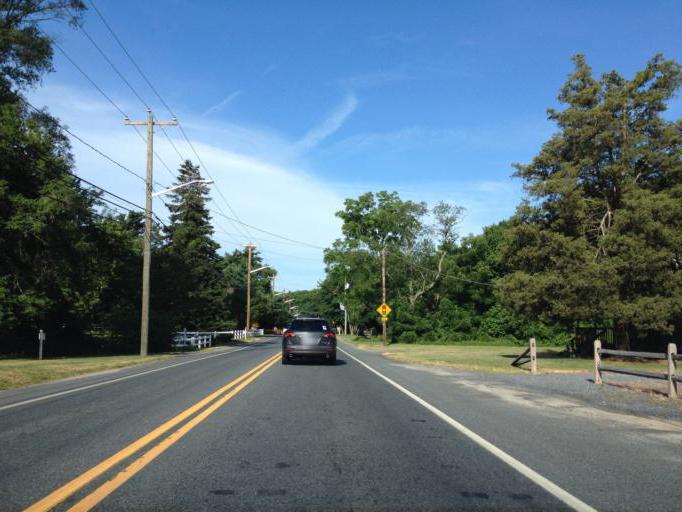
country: US
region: Delaware
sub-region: Sussex County
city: Millsboro
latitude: 38.5475
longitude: -75.2398
